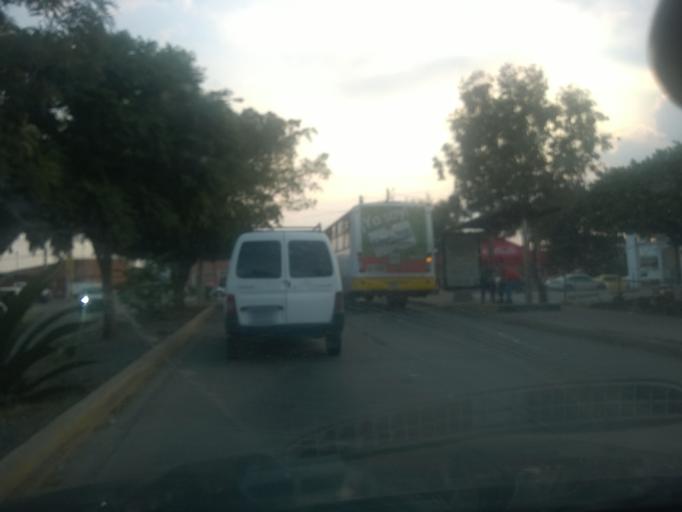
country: MX
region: Guanajuato
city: Leon
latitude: 21.0975
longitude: -101.6368
